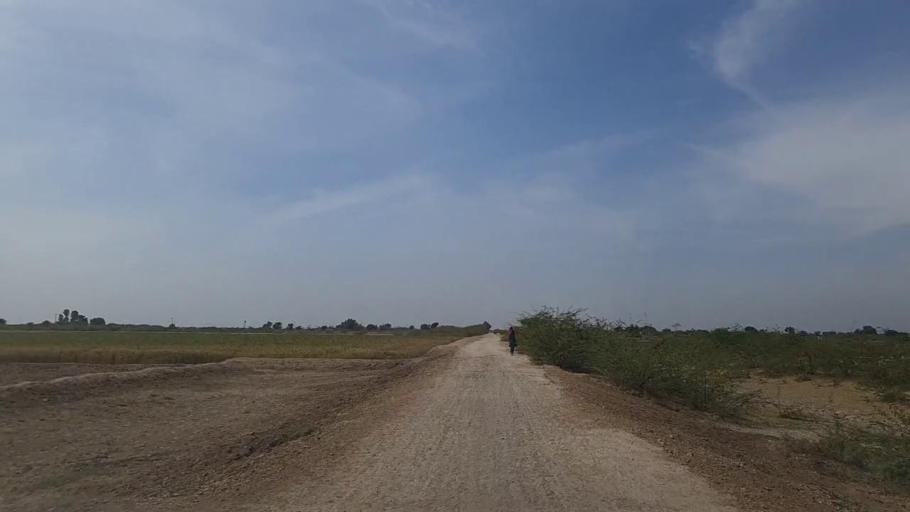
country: PK
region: Sindh
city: Kunri
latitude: 25.2127
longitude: 69.4921
